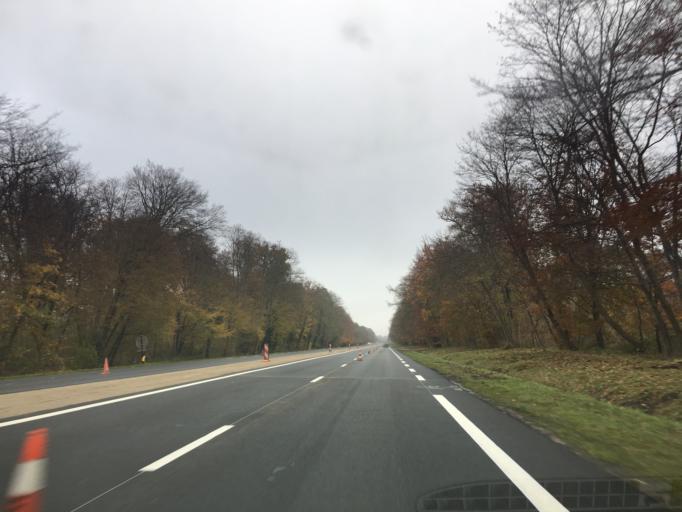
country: FR
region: Ile-de-France
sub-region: Departement de Seine-et-Marne
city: Avon
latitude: 48.3964
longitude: 2.7139
